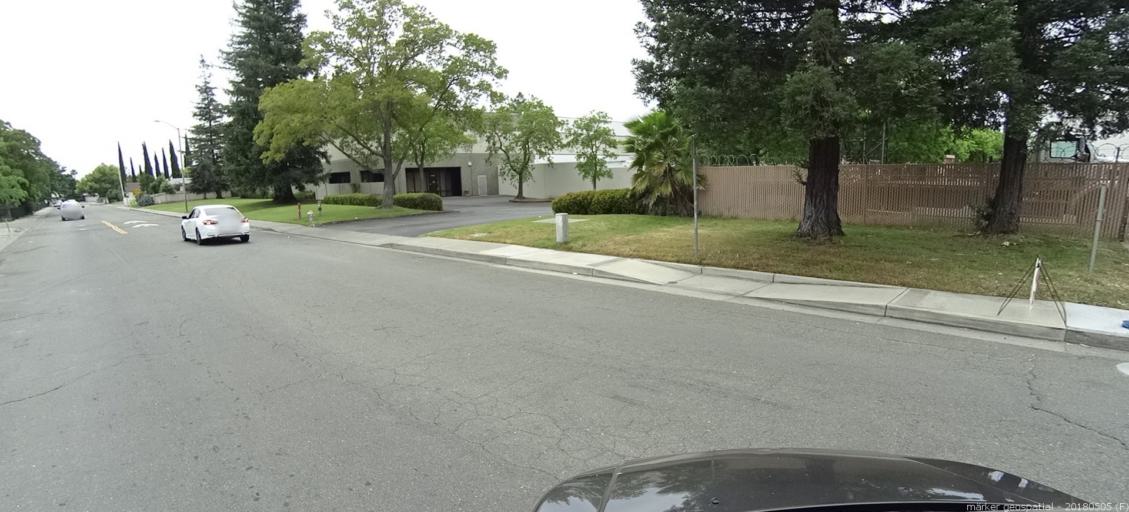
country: US
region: California
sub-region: Sacramento County
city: Rio Linda
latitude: 38.6542
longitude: -121.4661
